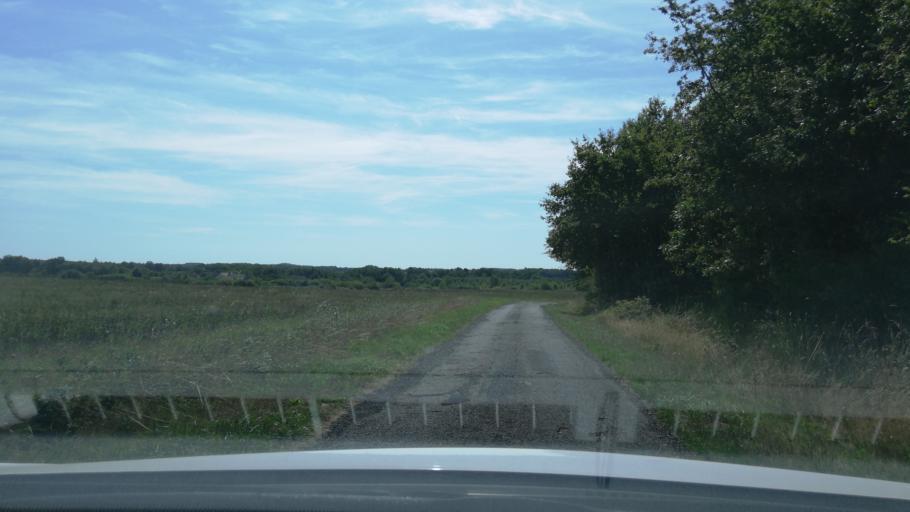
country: FR
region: Centre
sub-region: Departement d'Indre-et-Loire
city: Mazieres-de-Touraine
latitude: 47.3926
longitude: 0.4498
